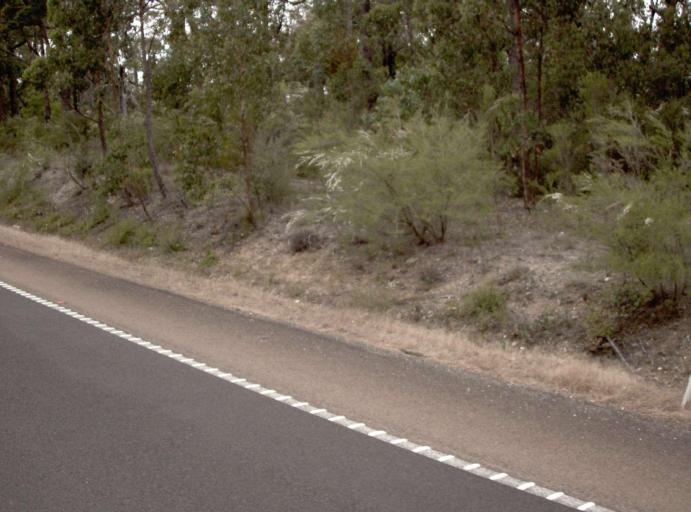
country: AU
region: Victoria
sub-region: East Gippsland
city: Lakes Entrance
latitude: -37.7152
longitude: 147.9627
